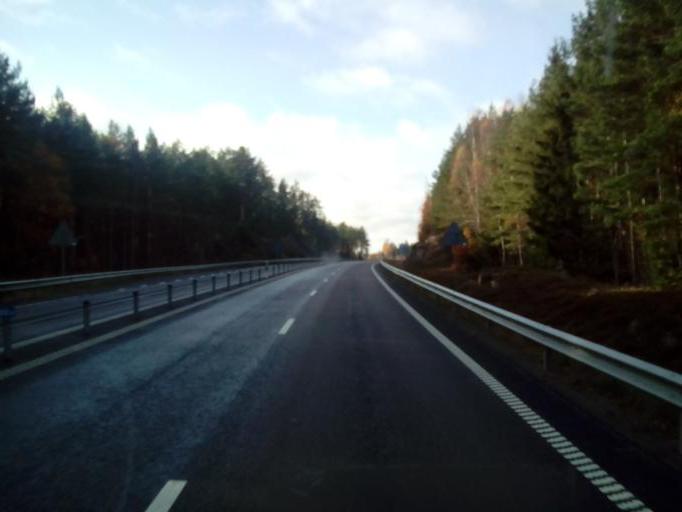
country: SE
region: Kalmar
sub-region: Vimmerby Kommun
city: Vimmerby
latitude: 57.6702
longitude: 15.9271
